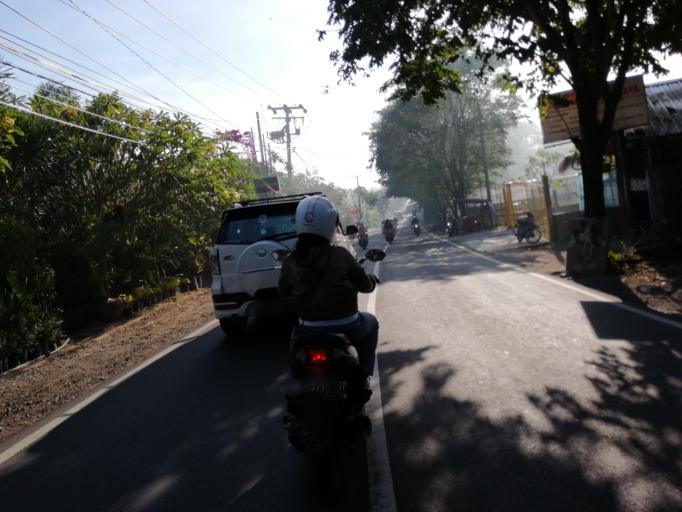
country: ID
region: Bali
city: Banjar Gunungpande
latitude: -8.6364
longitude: 115.1451
